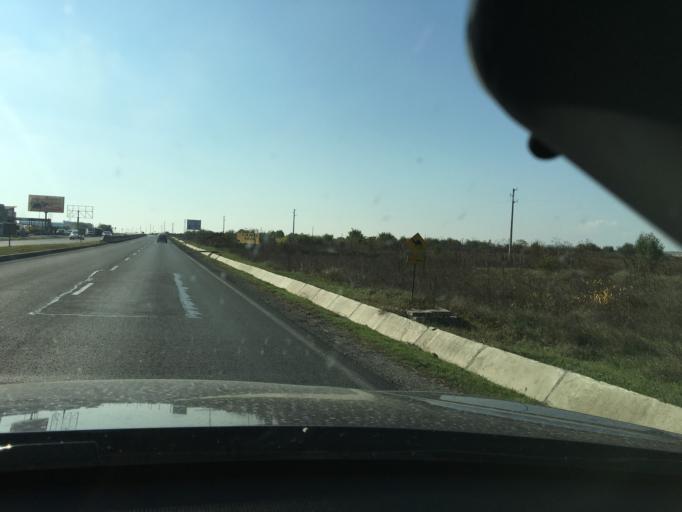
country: BG
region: Burgas
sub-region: Obshtina Nesebur
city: Ravda
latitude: 42.6577
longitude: 27.6835
